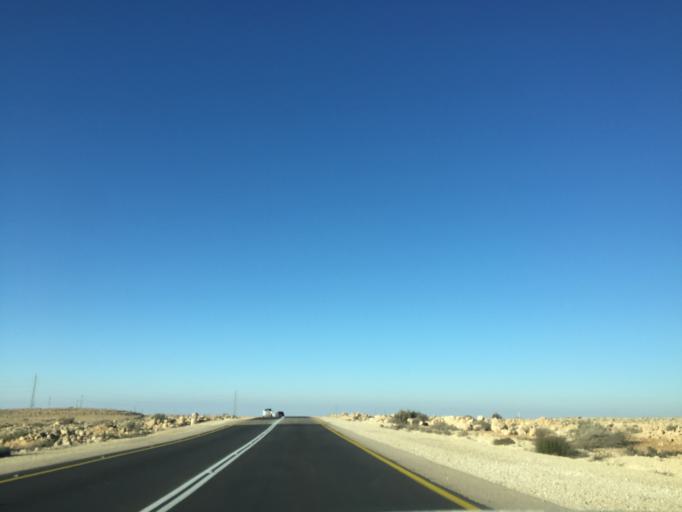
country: IL
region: Southern District
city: Mitzpe Ramon
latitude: 30.7186
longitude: 34.7780
